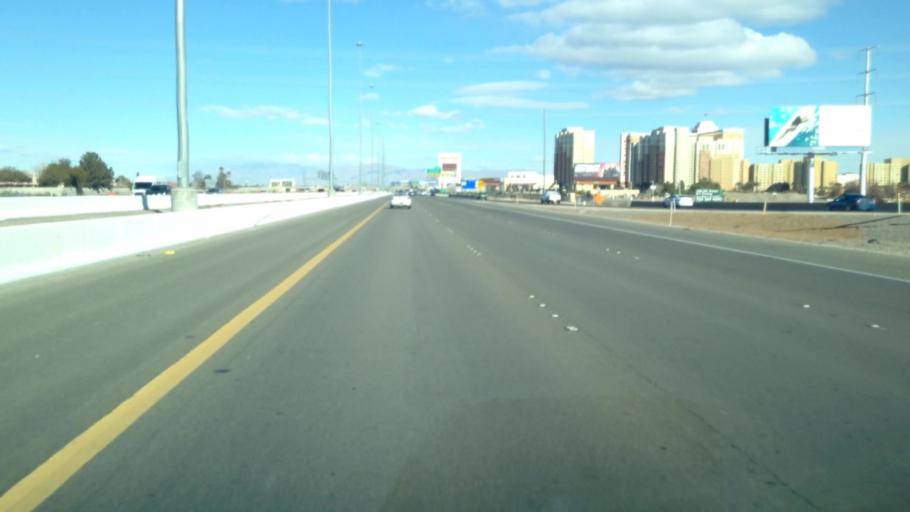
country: US
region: Nevada
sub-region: Clark County
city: Enterprise
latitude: 36.0010
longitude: -115.1805
